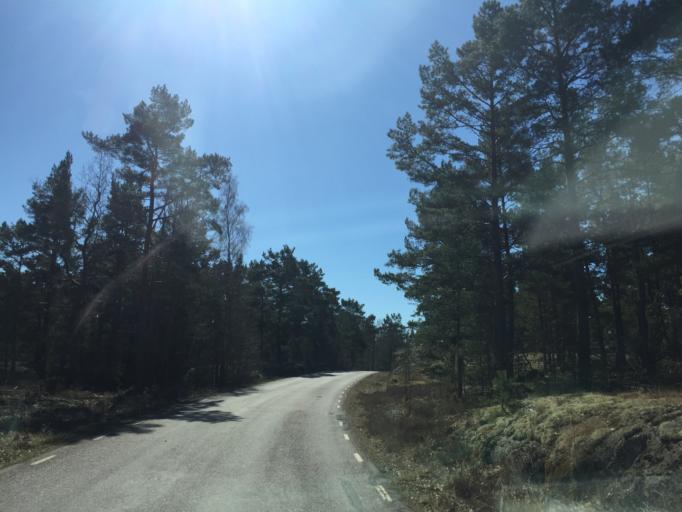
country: SE
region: Kalmar
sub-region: Oskarshamns Kommun
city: Oskarshamn
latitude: 57.2355
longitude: 16.4800
